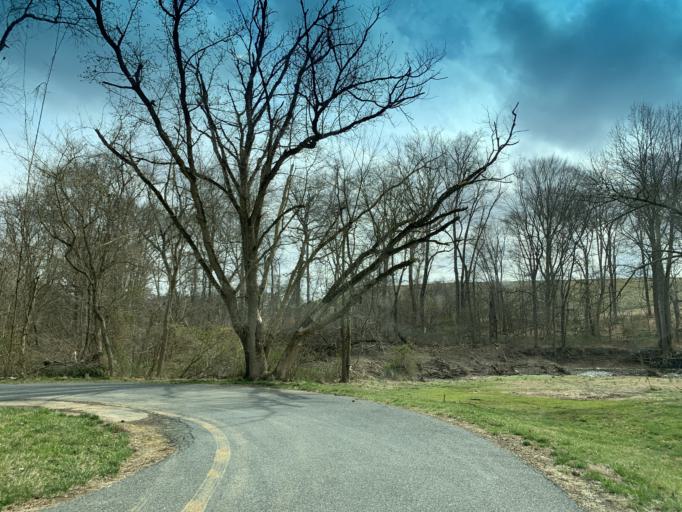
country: US
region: Maryland
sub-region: Harford County
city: North Bel Air
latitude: 39.5203
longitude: -76.3705
